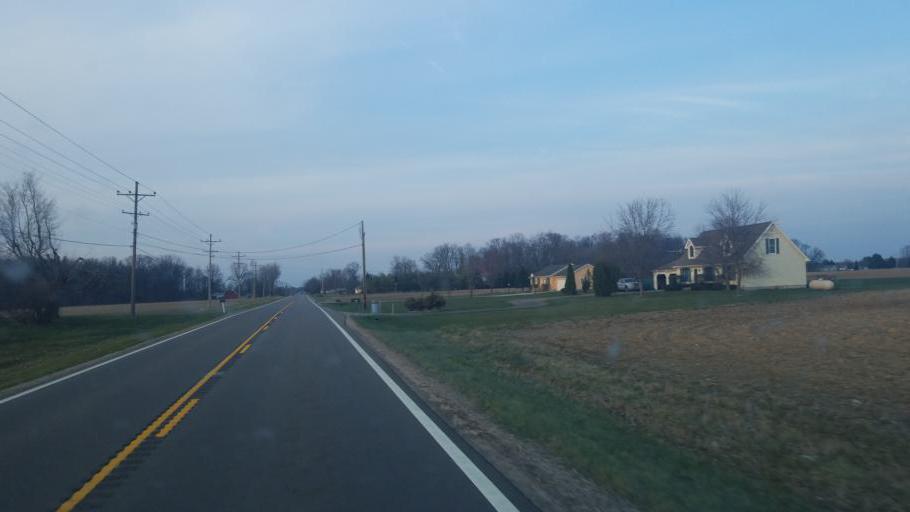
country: US
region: Ohio
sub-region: Marion County
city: Prospect
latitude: 40.5101
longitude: -83.1735
